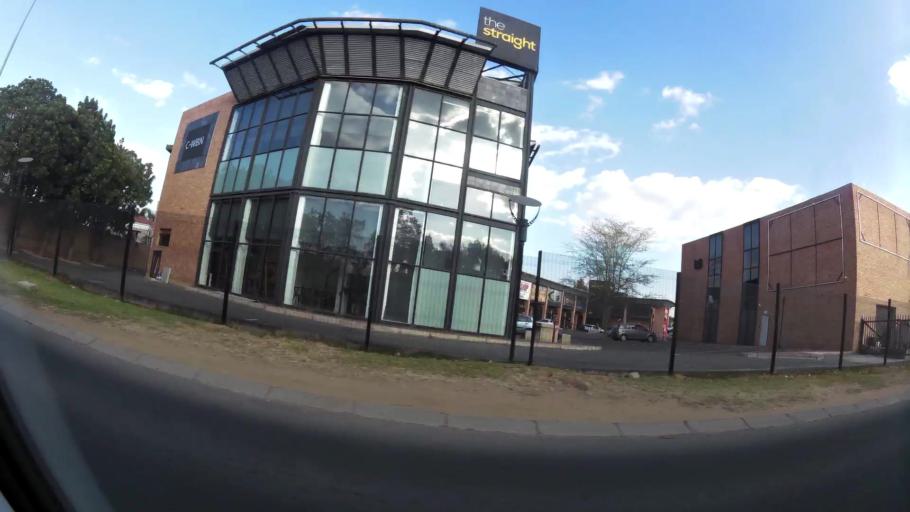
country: ZA
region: Gauteng
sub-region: City of Johannesburg Metropolitan Municipality
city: Diepsloot
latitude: -26.0210
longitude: 28.0173
